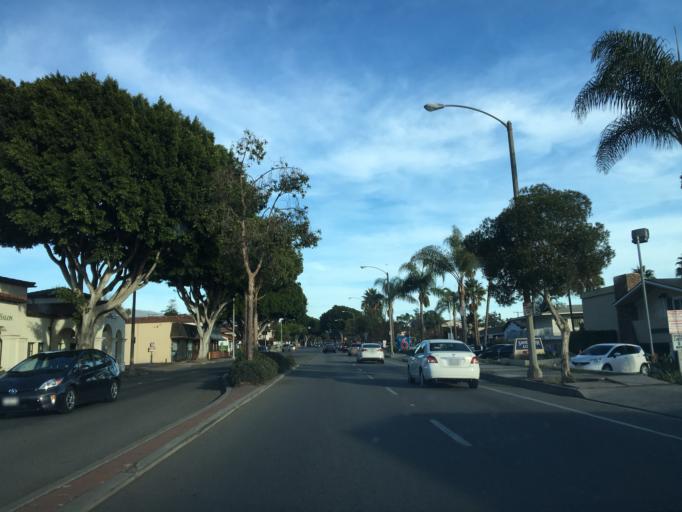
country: US
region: California
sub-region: Santa Barbara County
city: Mission Canyon
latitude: 34.4404
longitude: -119.7399
